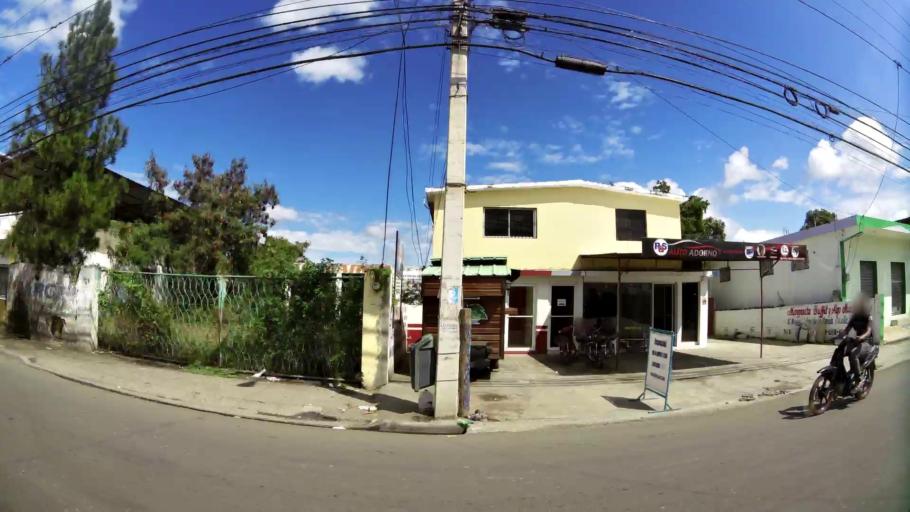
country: DO
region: La Vega
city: Concepcion de La Vega
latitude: 19.2295
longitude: -70.5309
